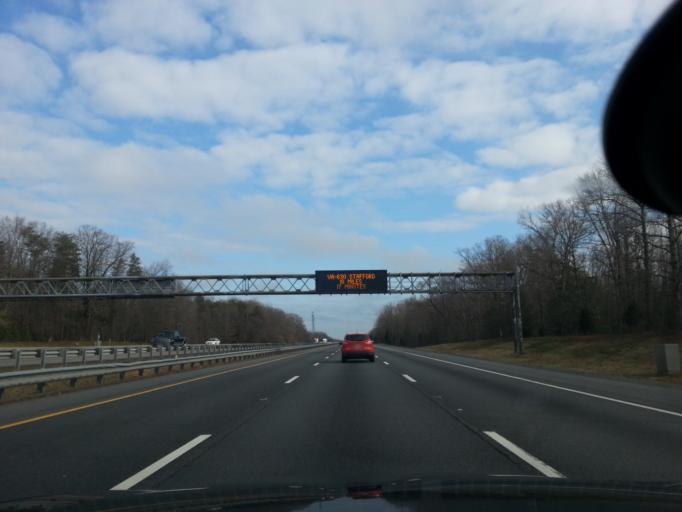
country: US
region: Virginia
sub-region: Spotsylvania County
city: Spotsylvania Courthouse
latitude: 38.1851
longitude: -77.5012
